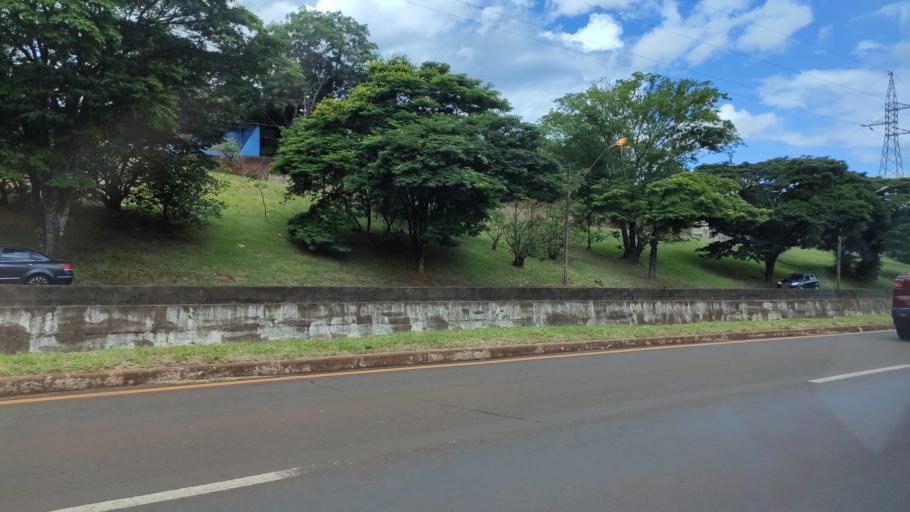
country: BR
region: Parana
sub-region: Londrina
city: Londrina
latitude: -23.3249
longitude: -51.1472
